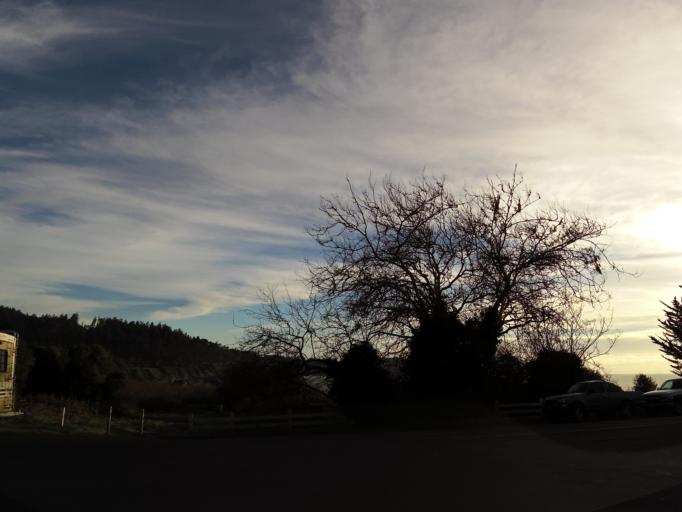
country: US
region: California
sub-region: Mendocino County
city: Fort Bragg
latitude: 39.3053
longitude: -123.7983
